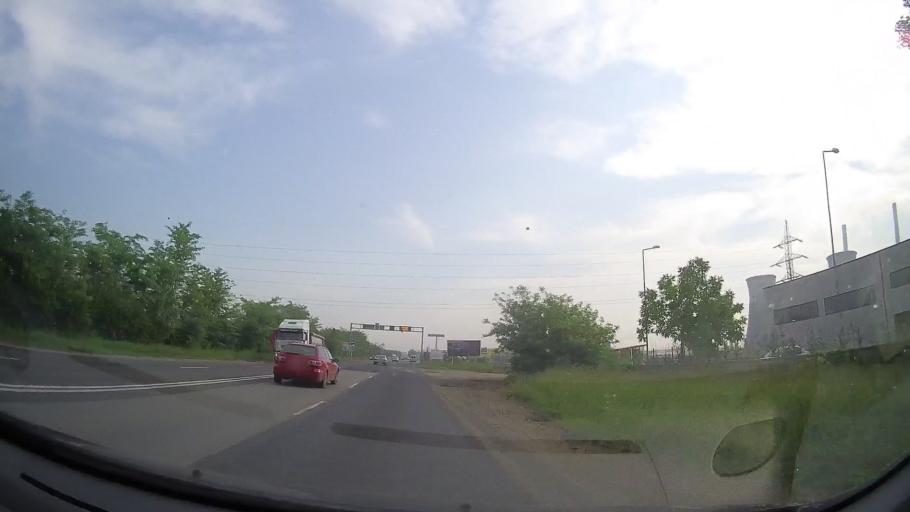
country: RO
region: Timis
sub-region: Comuna Giroc
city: Chisoda
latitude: 45.7093
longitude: 21.1895
